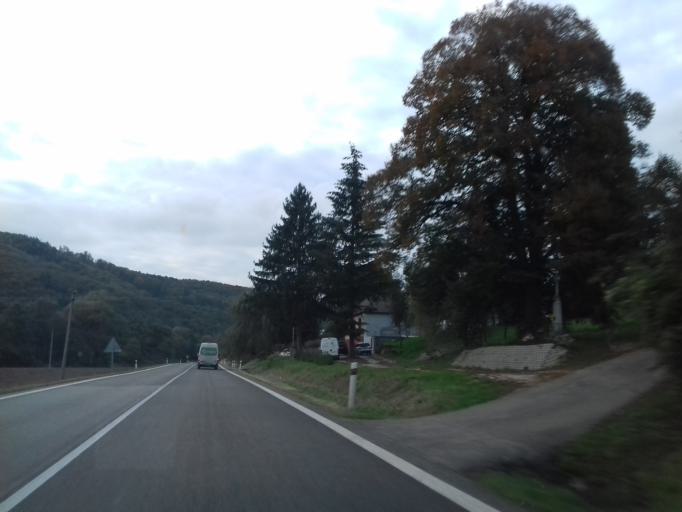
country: SK
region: Trenciansky
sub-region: Okres Trencin
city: Trencin
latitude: 48.9242
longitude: 17.9453
